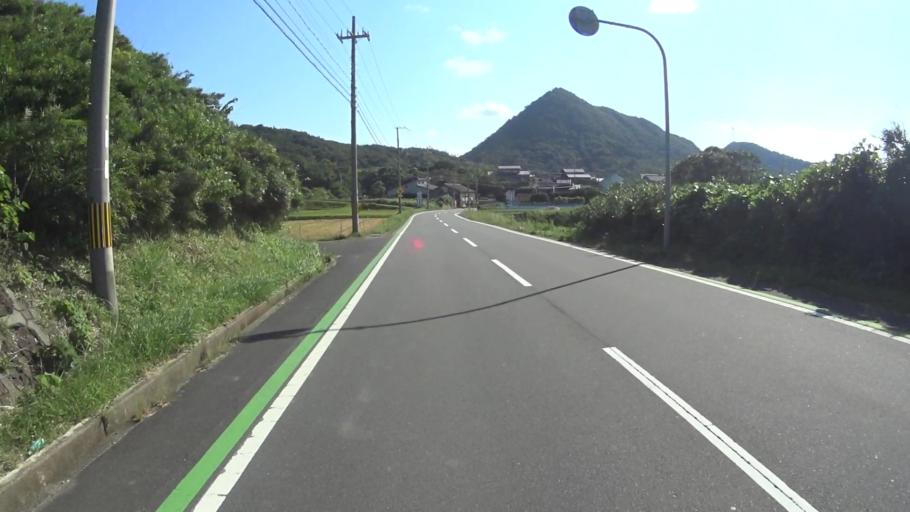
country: JP
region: Kyoto
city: Miyazu
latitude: 35.7227
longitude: 135.0839
